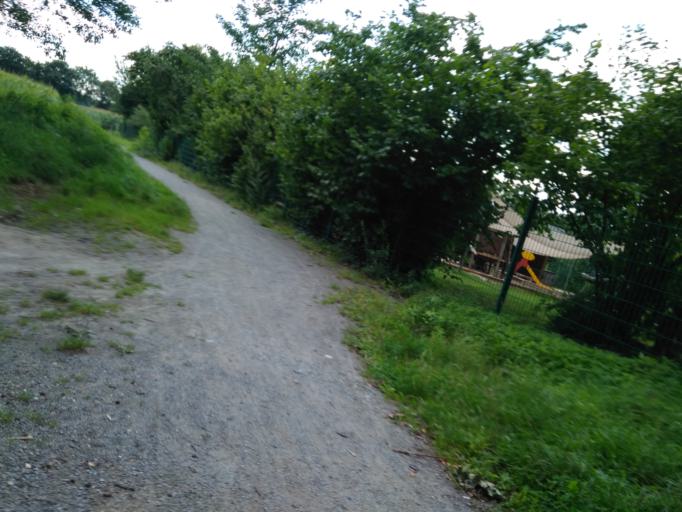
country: DE
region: North Rhine-Westphalia
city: Dorsten
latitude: 51.7115
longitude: 6.9674
